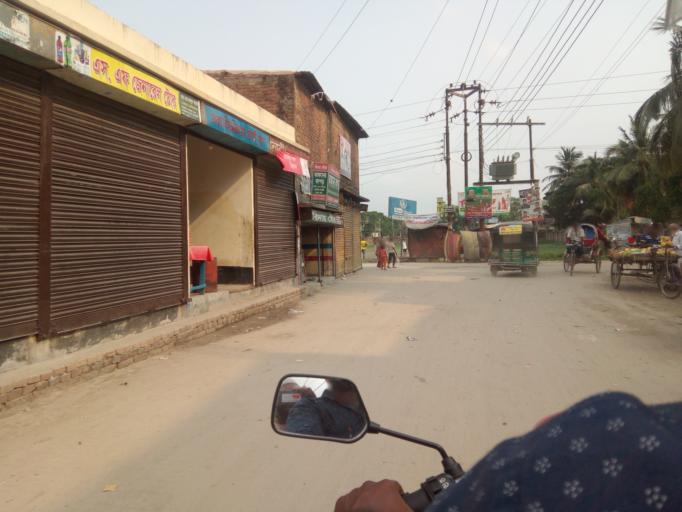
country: BD
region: Dhaka
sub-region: Dhaka
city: Dhaka
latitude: 23.7076
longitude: 90.4582
